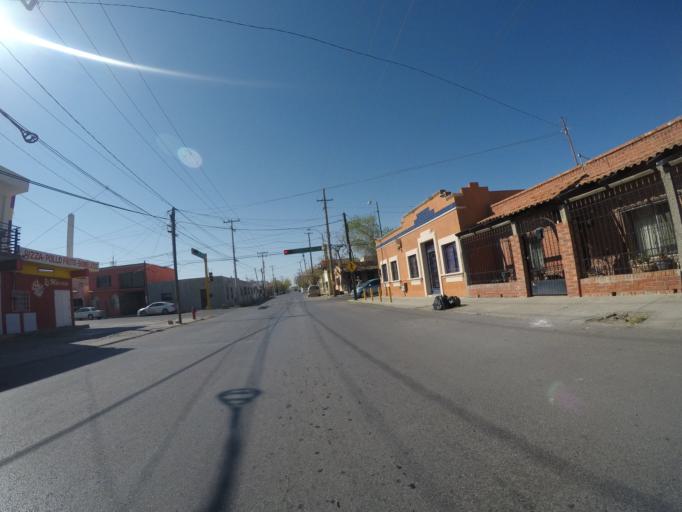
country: MX
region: Chihuahua
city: Ciudad Juarez
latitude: 31.7414
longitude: -106.4737
